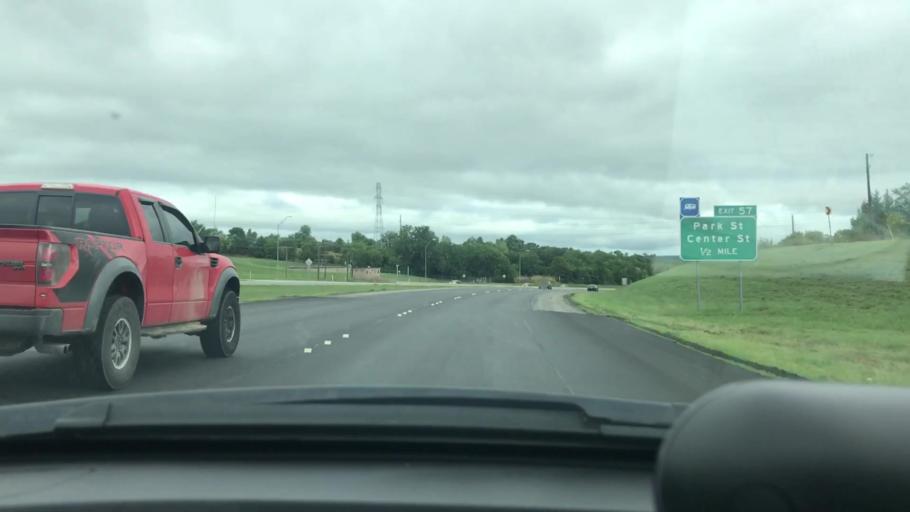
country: US
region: Texas
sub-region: Grayson County
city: Sherman
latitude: 33.6031
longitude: -96.6091
